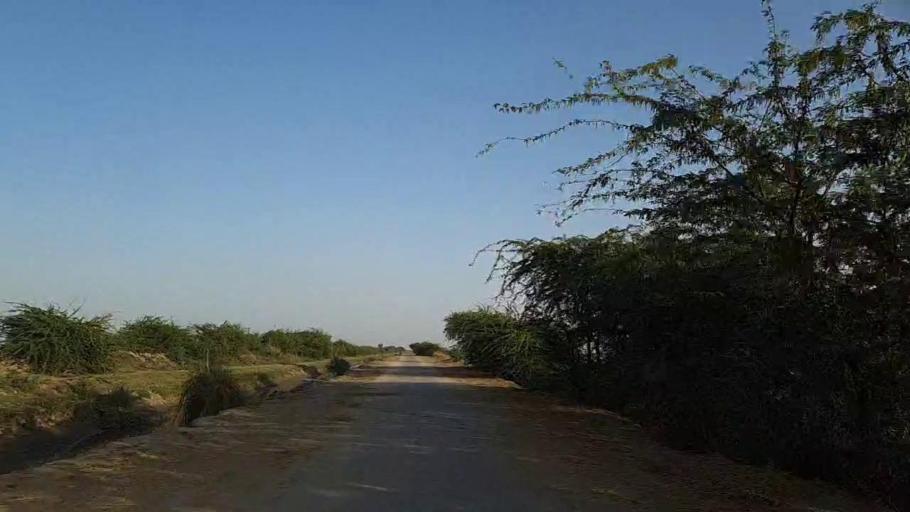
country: PK
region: Sindh
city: Jati
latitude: 24.4130
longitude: 68.3455
